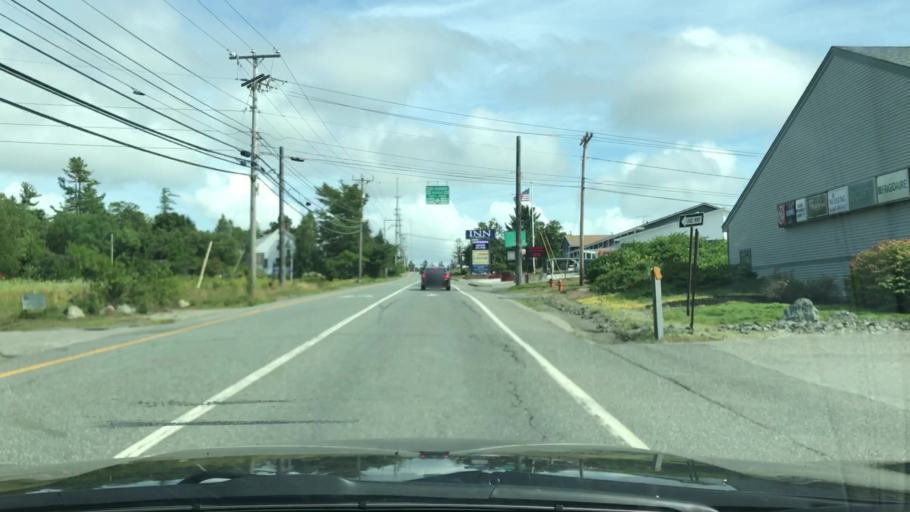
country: US
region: Maine
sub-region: Hancock County
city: Ellsworth
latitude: 44.5266
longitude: -68.4012
